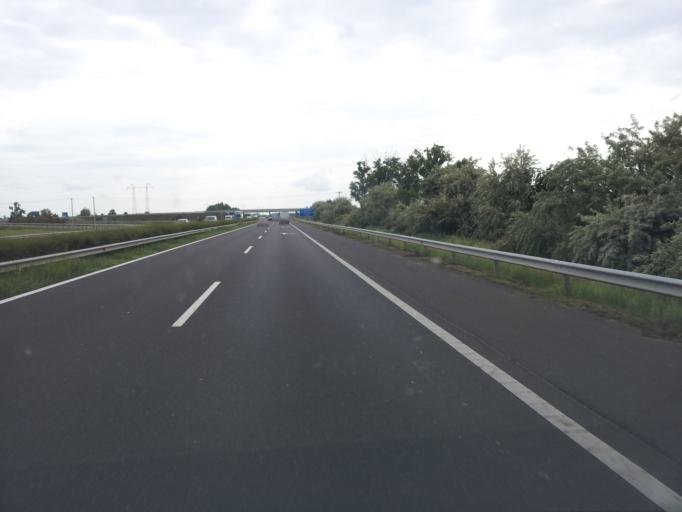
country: HU
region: Heves
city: Fuzesabony
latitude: 47.7305
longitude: 20.4074
